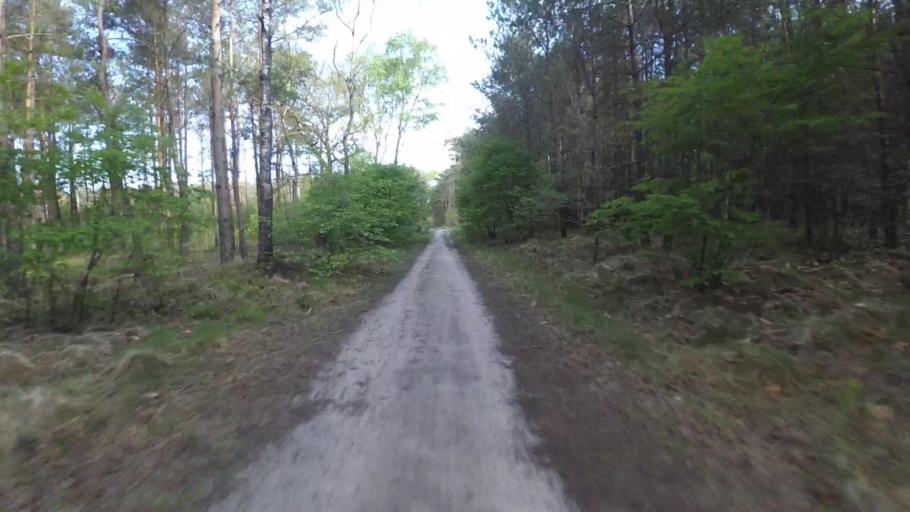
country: NL
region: Utrecht
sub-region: Gemeente Utrechtse Heuvelrug
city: Driebergen-Rijsenburg
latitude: 52.1025
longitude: 5.3140
